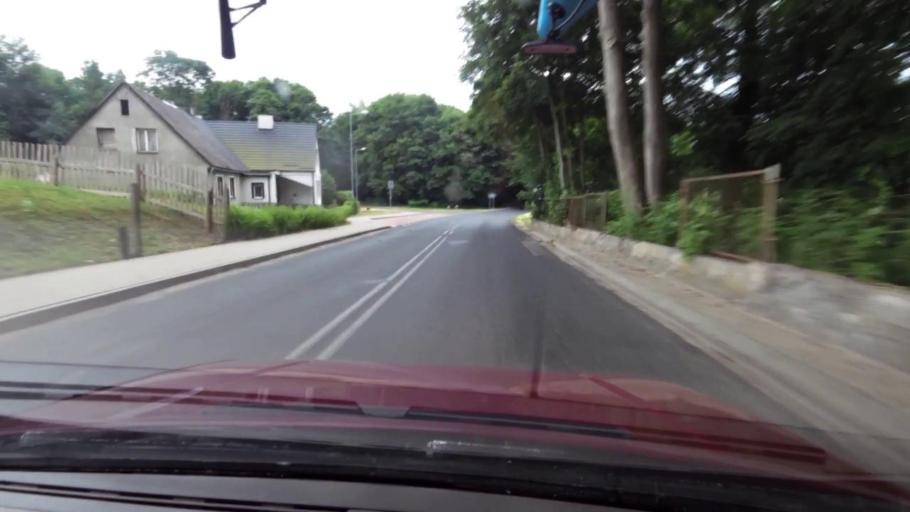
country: PL
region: West Pomeranian Voivodeship
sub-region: Powiat koszalinski
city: Polanow
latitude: 54.1386
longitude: 16.5222
